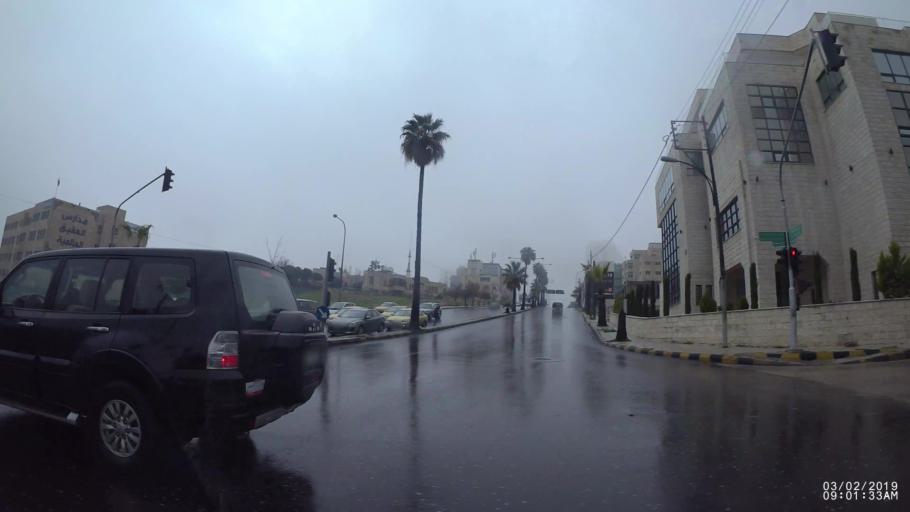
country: JO
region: Amman
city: Amman
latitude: 31.9644
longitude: 35.8840
